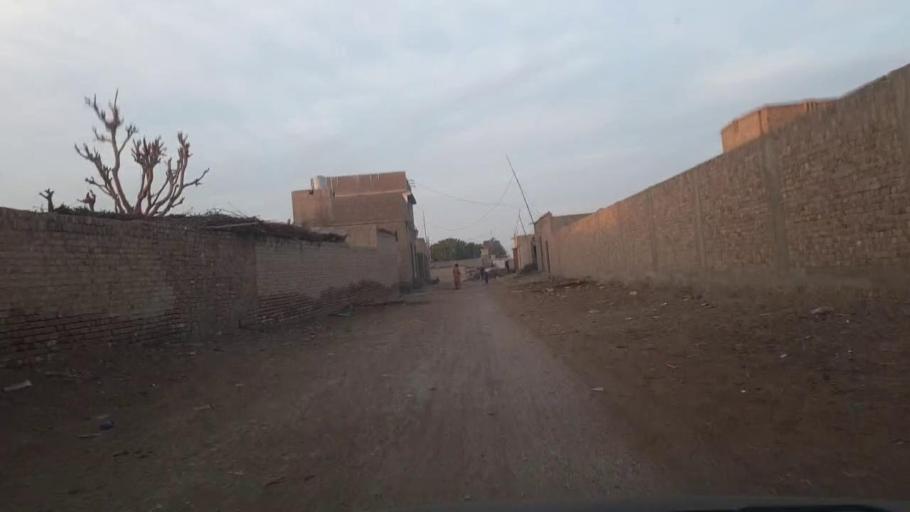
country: PK
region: Sindh
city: Shahpur Chakar
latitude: 26.0741
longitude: 68.5322
